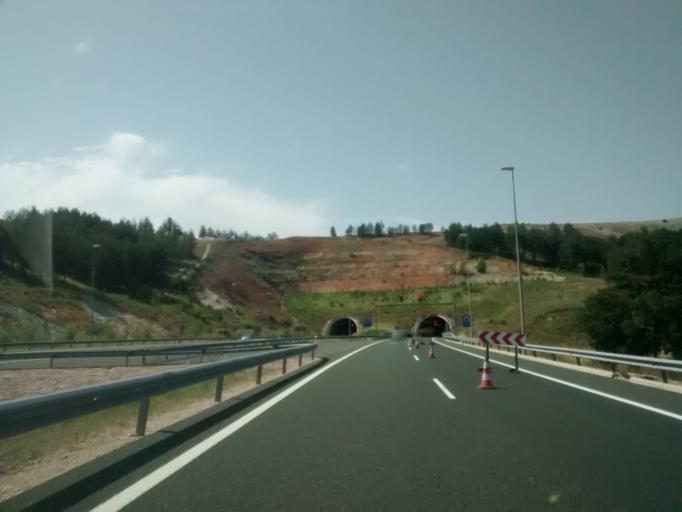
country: ES
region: Castille and Leon
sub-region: Provincia de Palencia
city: Alar del Rey
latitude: 42.6873
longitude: -4.2994
